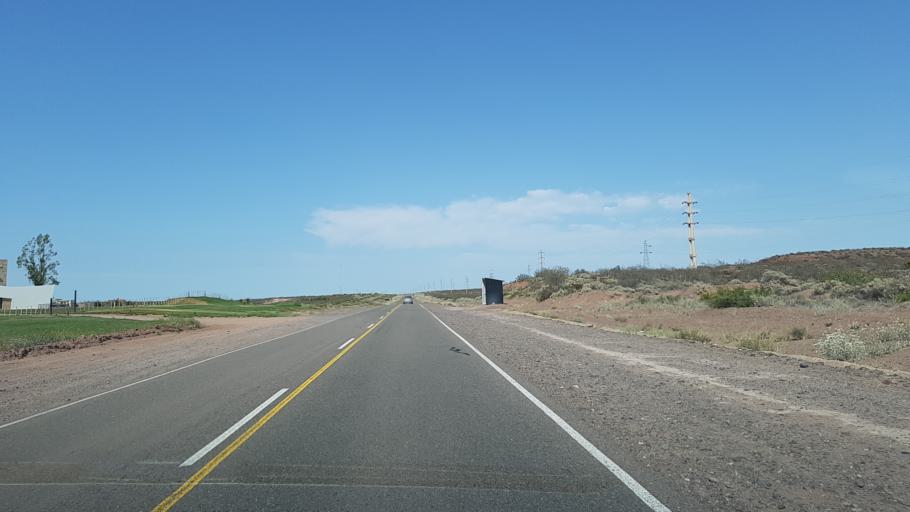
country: AR
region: Neuquen
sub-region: Departamento de Picun Leufu
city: Picun Leufu
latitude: -39.3314
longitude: -68.9723
